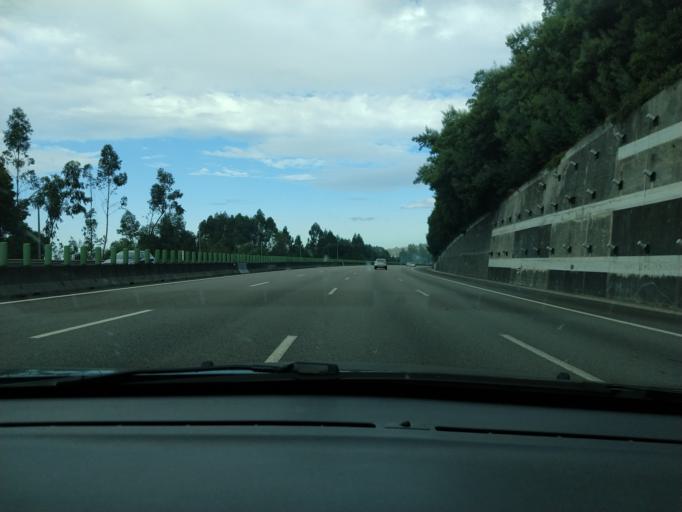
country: PT
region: Porto
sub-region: Vila Nova de Gaia
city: Perozinho
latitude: 41.0542
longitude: -8.5755
